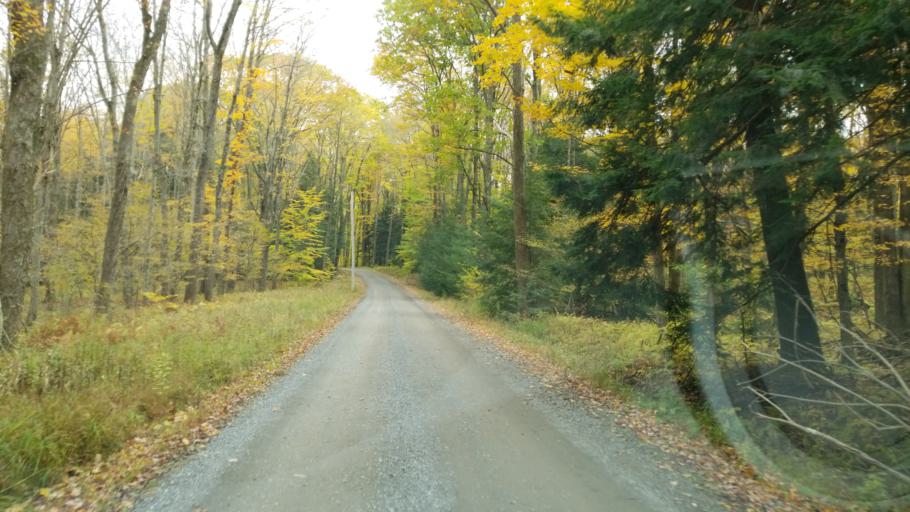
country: US
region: Pennsylvania
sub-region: Clearfield County
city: Clearfield
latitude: 41.1992
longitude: -78.4185
